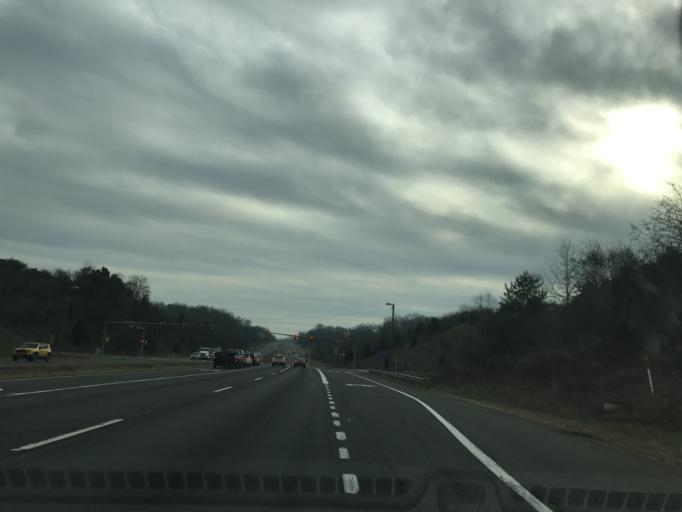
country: US
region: Virginia
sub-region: City of Manassas
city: Manassas
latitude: 38.7239
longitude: -77.4976
